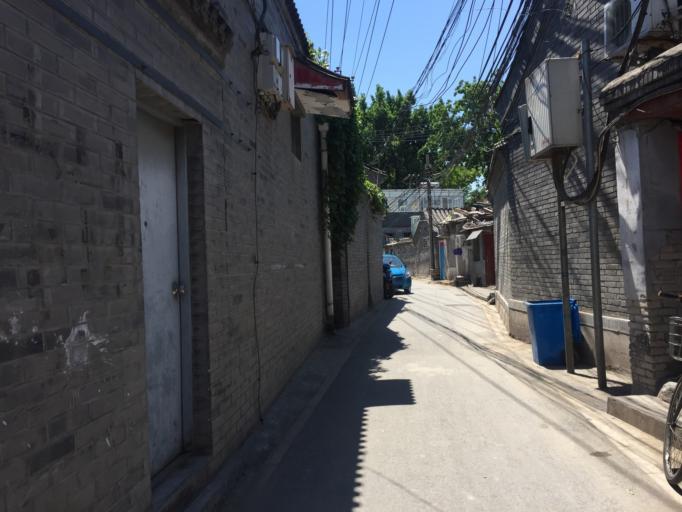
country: CN
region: Beijing
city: Jingshan
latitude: 39.9314
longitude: 116.3875
